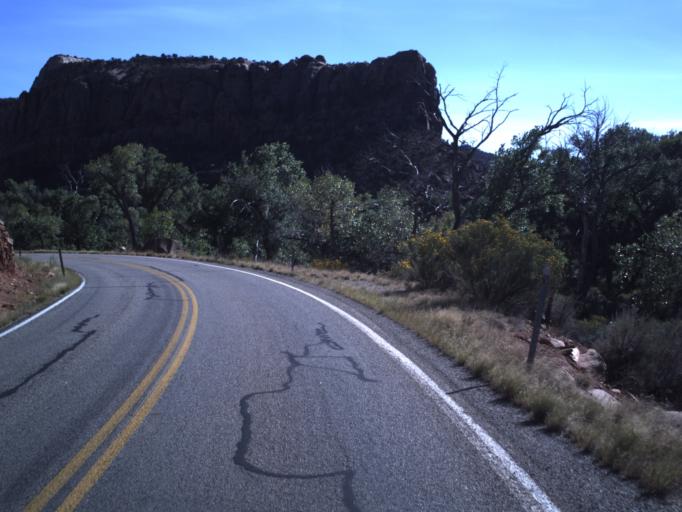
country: US
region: Utah
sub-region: San Juan County
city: Monticello
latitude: 38.0404
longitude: -109.5533
